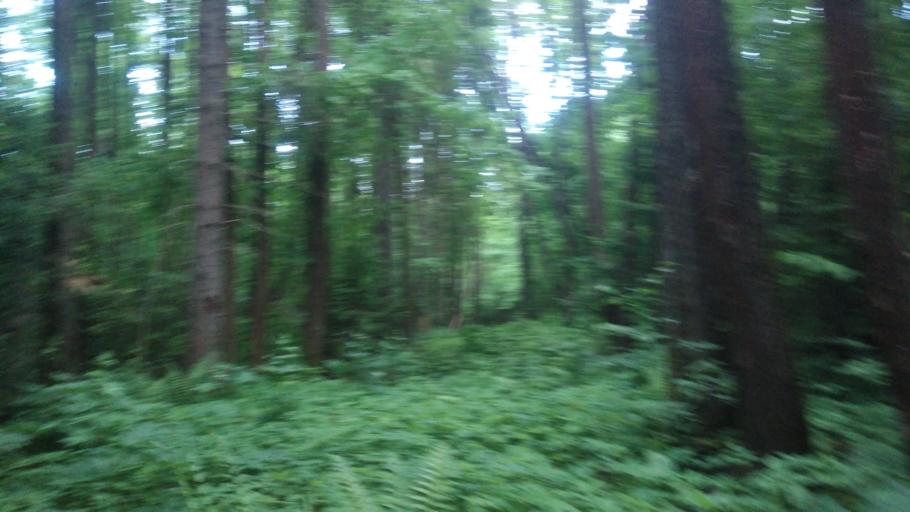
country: RU
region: Perm
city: Ferma
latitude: 57.9646
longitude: 56.3430
